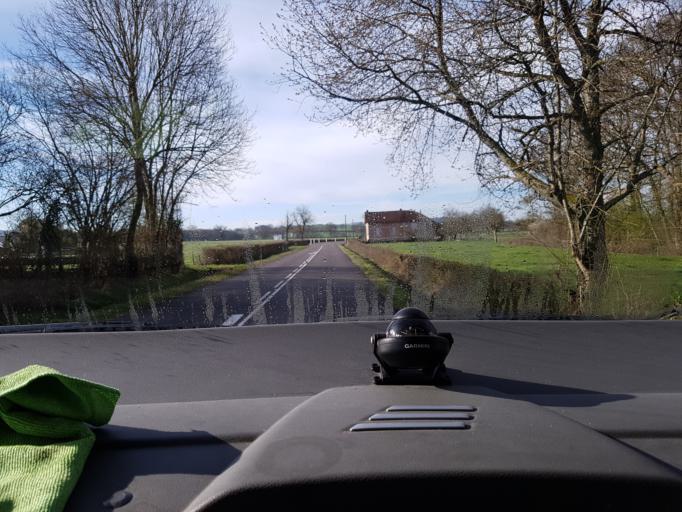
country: FR
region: Bourgogne
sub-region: Departement de Saone-et-Loire
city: Etang-sur-Arroux
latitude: 46.8470
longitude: 4.1973
